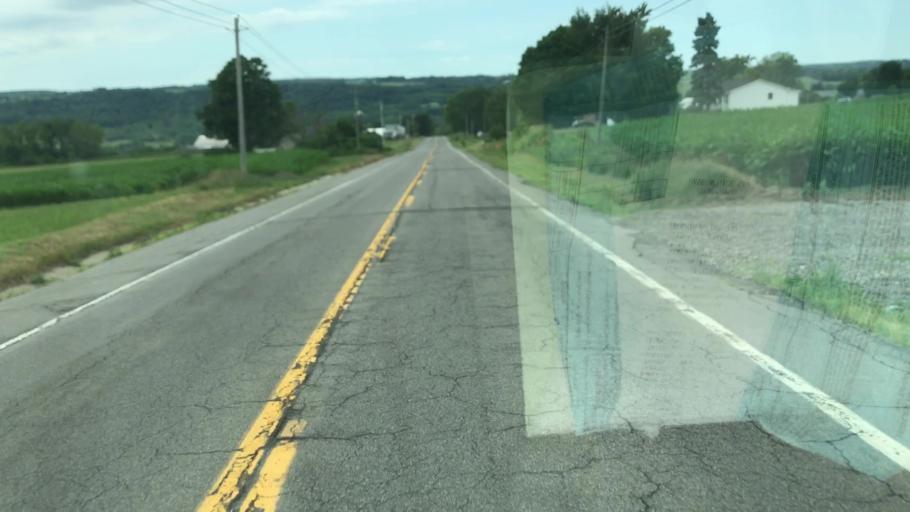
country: US
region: New York
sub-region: Onondaga County
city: Marcellus
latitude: 42.9333
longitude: -76.3121
